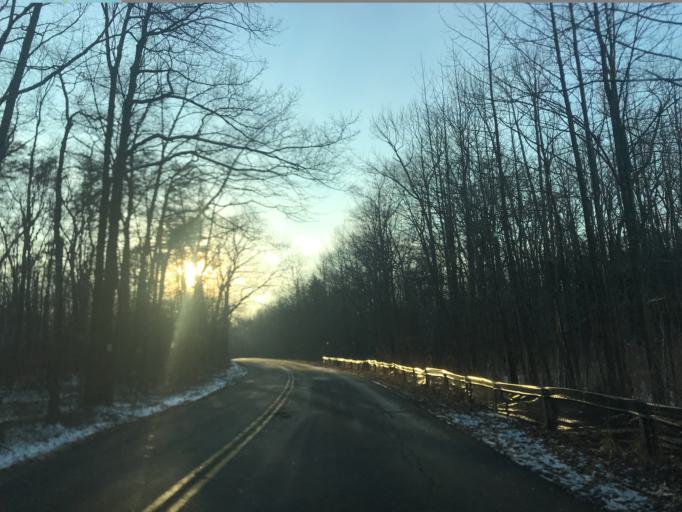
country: US
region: Maryland
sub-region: Harford County
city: Edgewood
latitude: 39.4347
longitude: -76.2562
